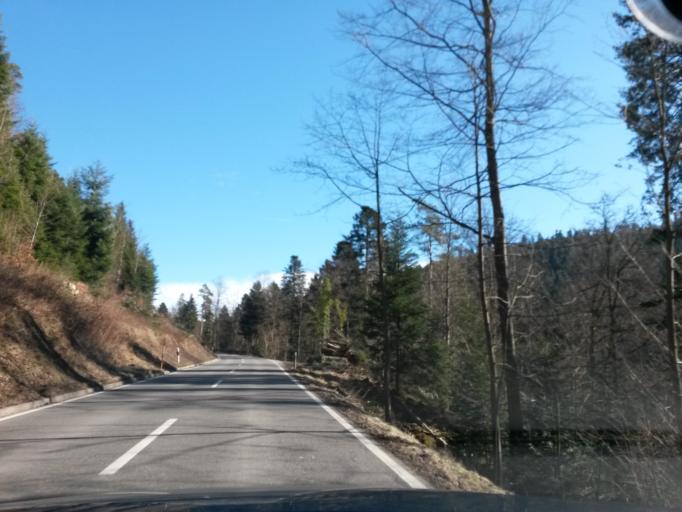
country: DE
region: Baden-Wuerttemberg
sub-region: Karlsruhe Region
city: Hofen an der Enz
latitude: 48.7977
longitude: 8.6083
